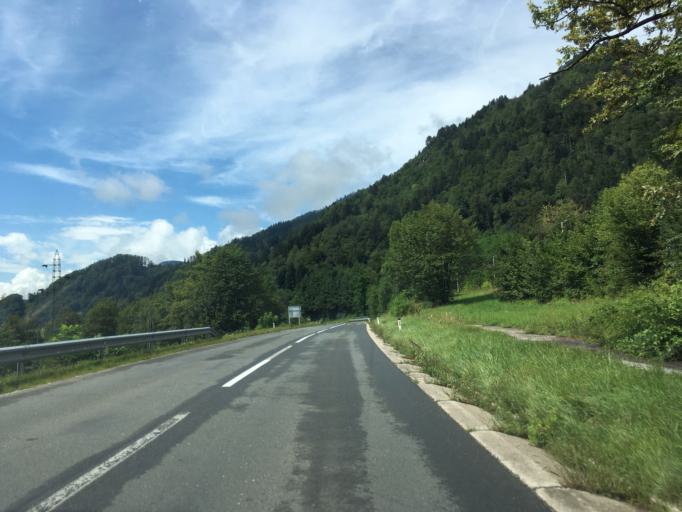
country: SI
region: Zirovnica
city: Zirovnica
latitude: 46.4122
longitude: 14.1279
